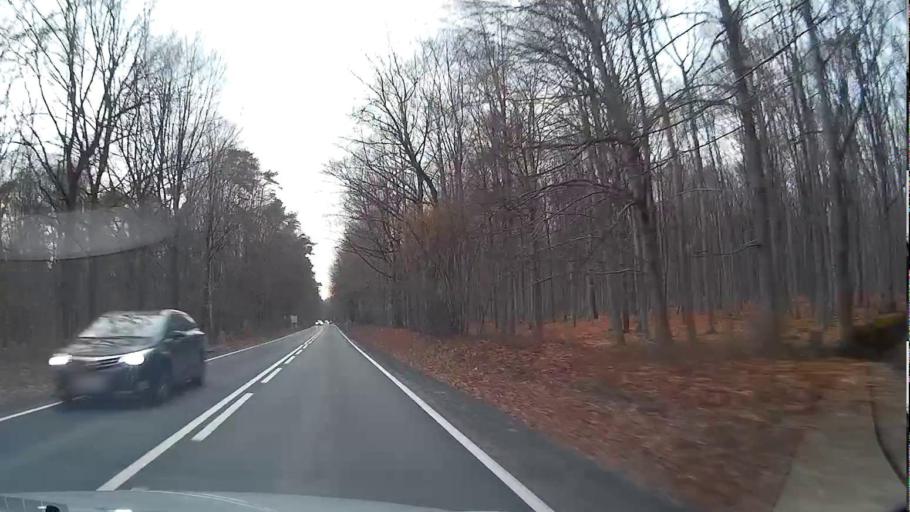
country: PL
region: Lesser Poland Voivodeship
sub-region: Powiat chrzanowski
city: Zagorze
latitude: 50.0716
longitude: 19.4095
